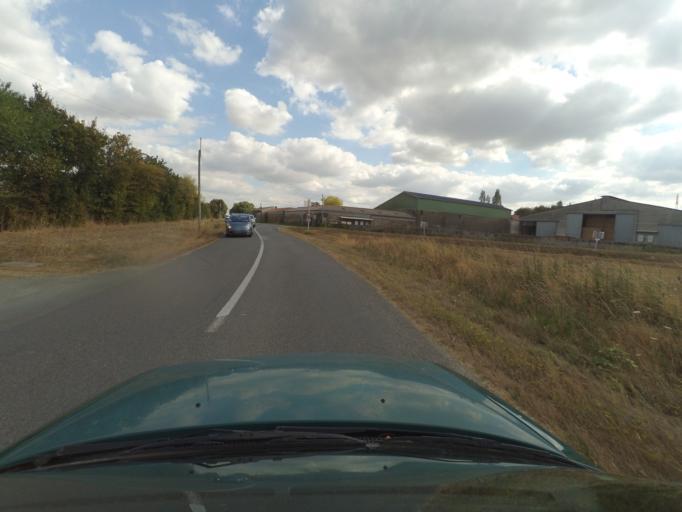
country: FR
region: Pays de la Loire
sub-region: Departement de la Loire-Atlantique
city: La Planche
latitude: 46.9971
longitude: -1.4552
